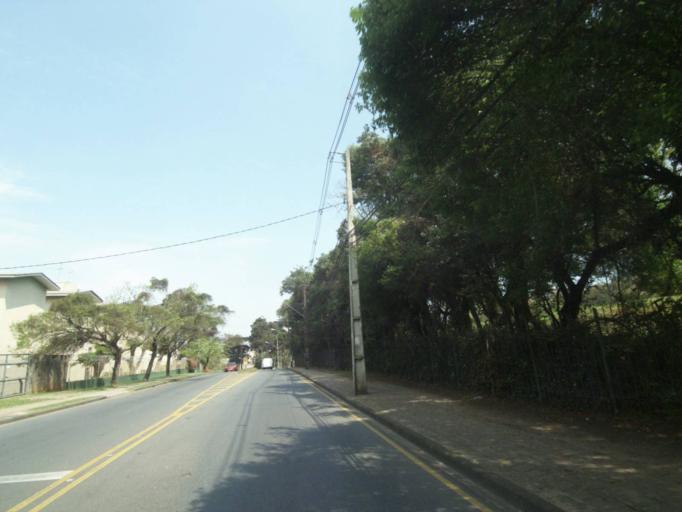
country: BR
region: Parana
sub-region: Curitiba
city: Curitiba
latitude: -25.4764
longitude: -49.3218
